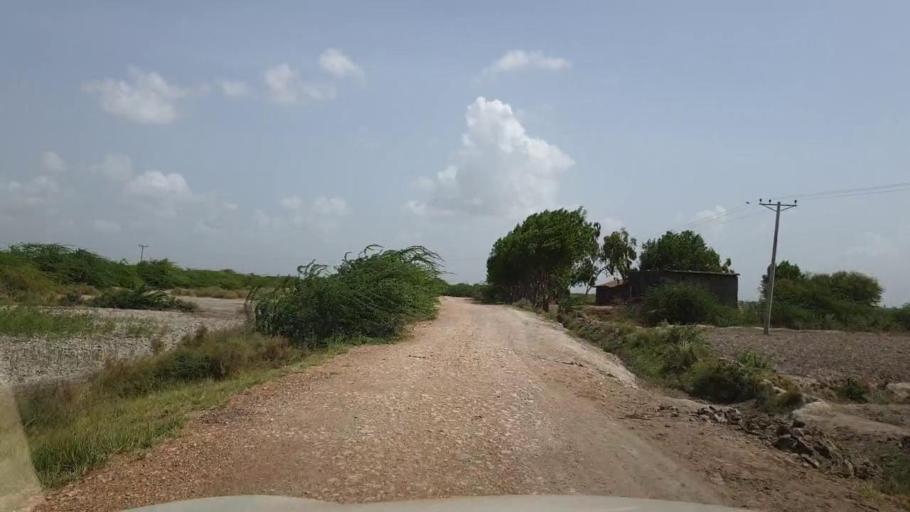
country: PK
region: Sindh
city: Kadhan
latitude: 24.4027
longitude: 68.7989
